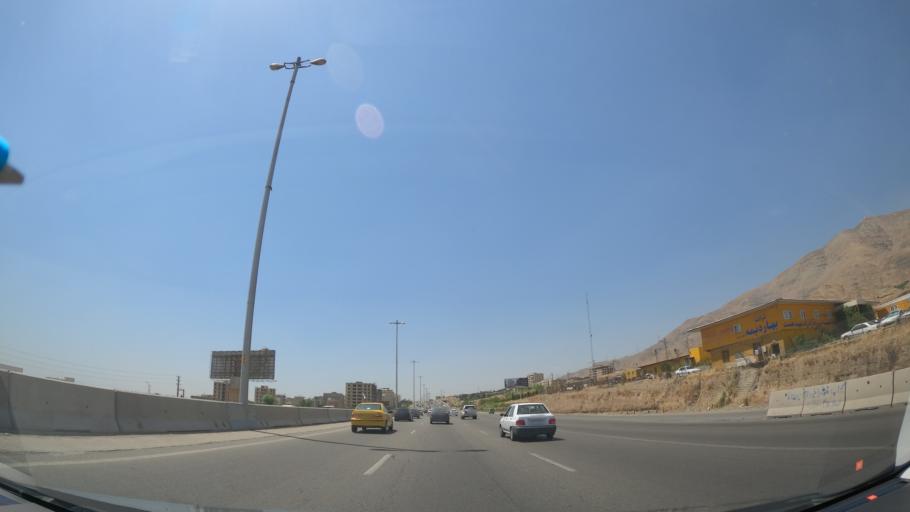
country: IR
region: Tehran
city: Shahr-e Qods
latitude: 35.7534
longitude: 51.0762
